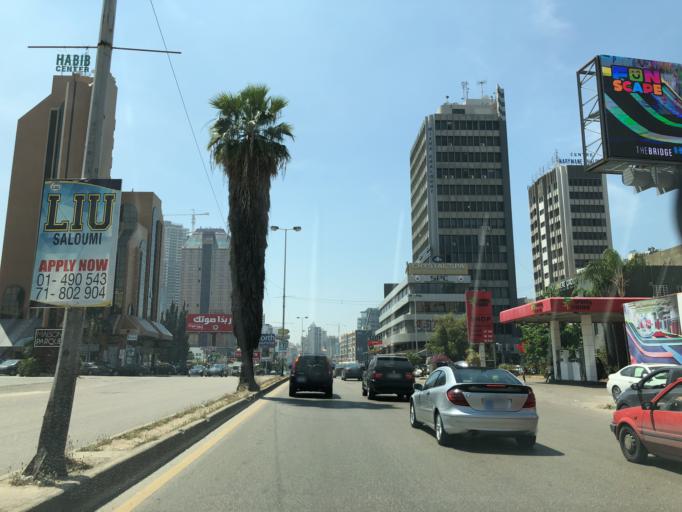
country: LB
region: Mont-Liban
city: Jdaidet el Matn
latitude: 33.8851
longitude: 35.5467
